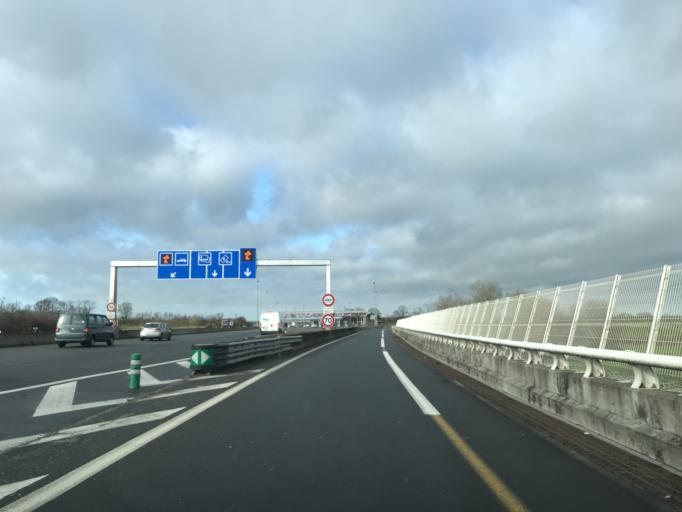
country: FR
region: Lower Normandy
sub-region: Departement du Calvados
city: Dozule
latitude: 49.2318
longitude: -0.0665
